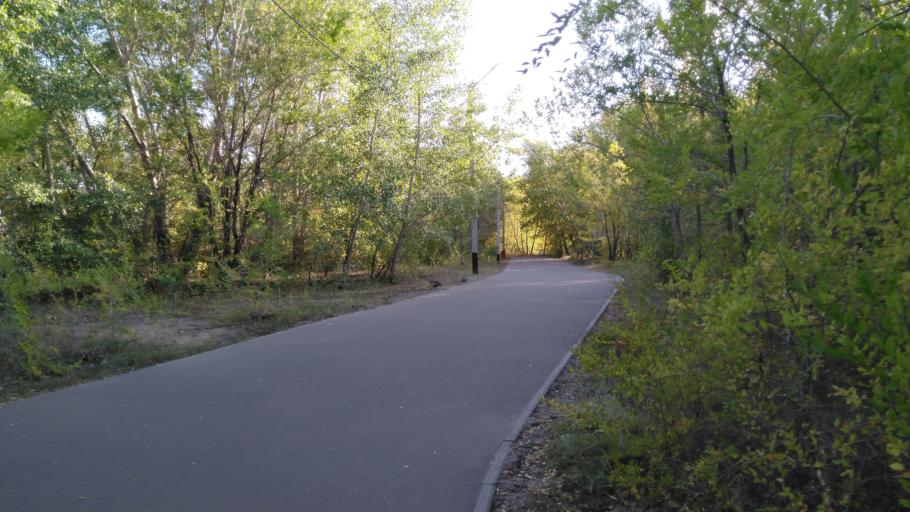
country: KZ
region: Pavlodar
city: Pavlodar
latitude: 52.2605
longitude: 76.9378
